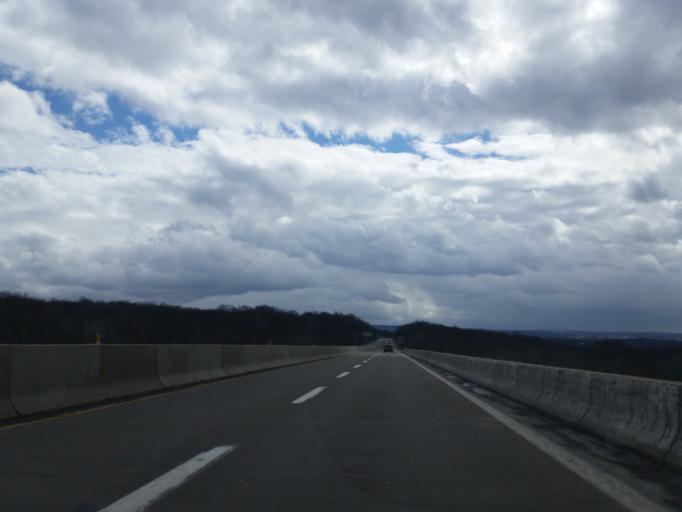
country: US
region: Pennsylvania
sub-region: Lackawanna County
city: Old Forge
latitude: 41.3753
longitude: -75.7205
